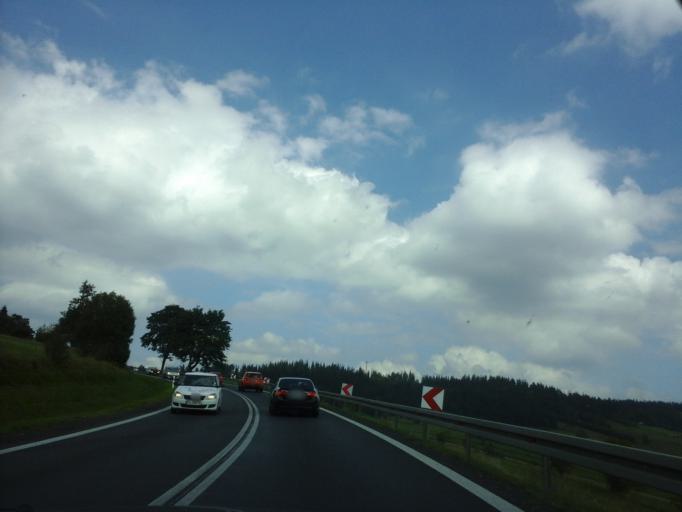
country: PL
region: Lesser Poland Voivodeship
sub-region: Powiat nowotarski
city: Klikuszowa
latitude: 49.5273
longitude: 19.9786
